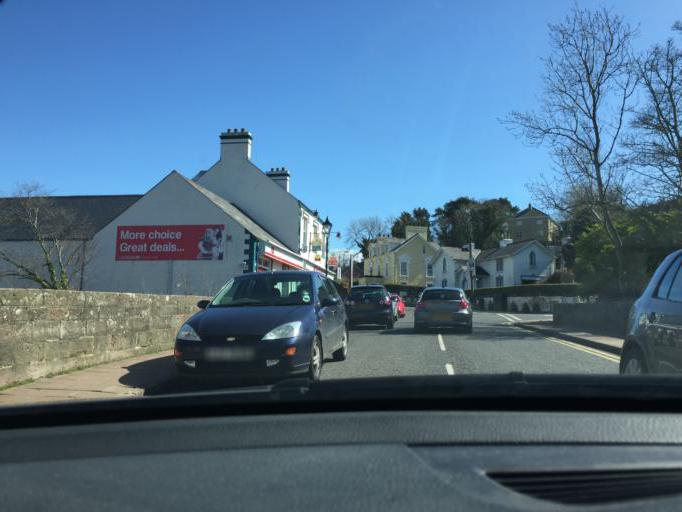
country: GB
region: Northern Ireland
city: Cushendall
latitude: 55.0806
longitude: -6.0634
